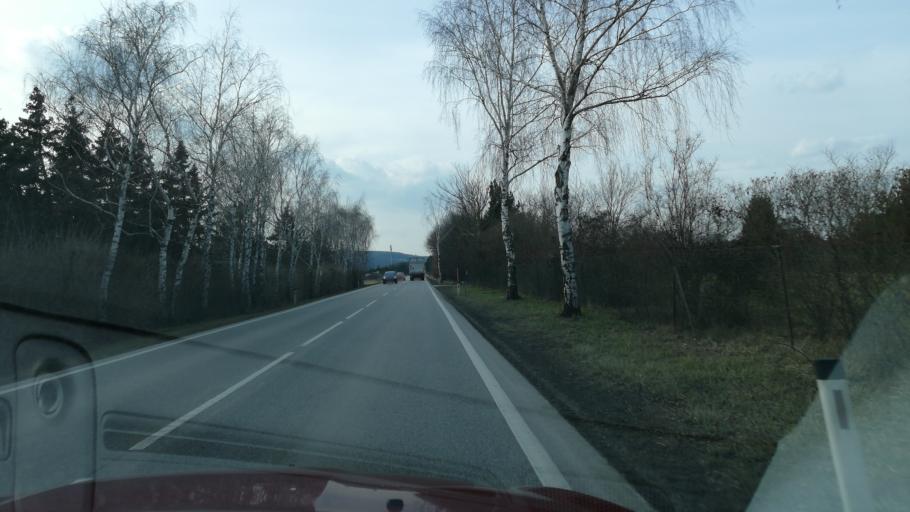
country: AT
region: Lower Austria
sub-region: Politischer Bezirk Tulln
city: Grafenworth
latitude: 48.3358
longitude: 15.8207
